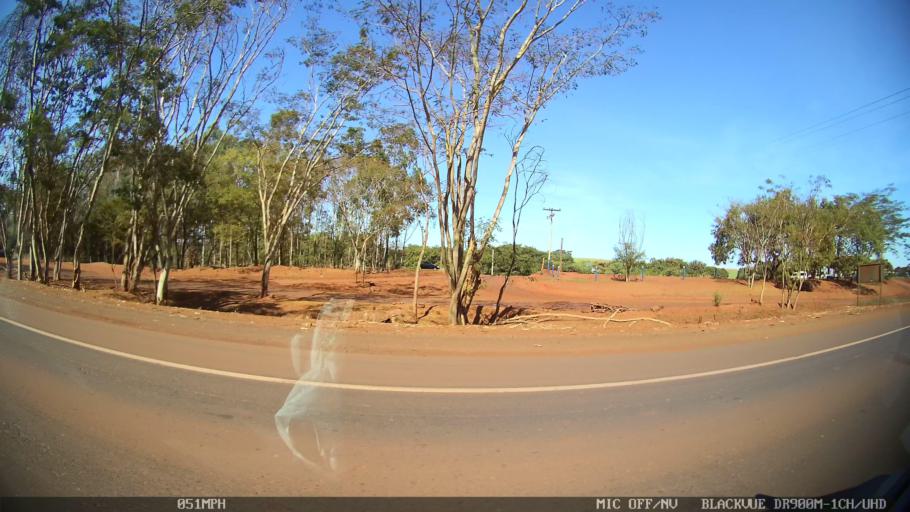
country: BR
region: Sao Paulo
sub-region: Barretos
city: Barretos
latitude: -20.4581
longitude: -48.4629
